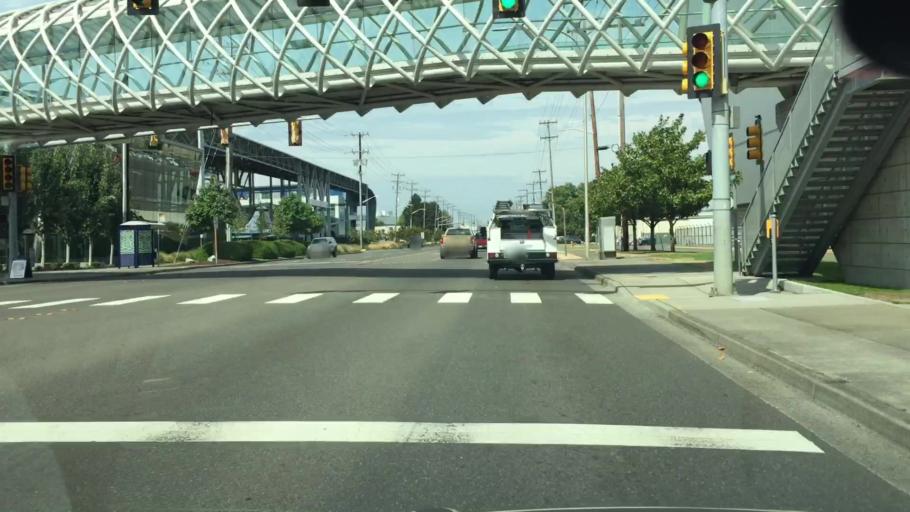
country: US
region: Washington
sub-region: King County
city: Boulevard Park
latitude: 47.5186
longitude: -122.2979
